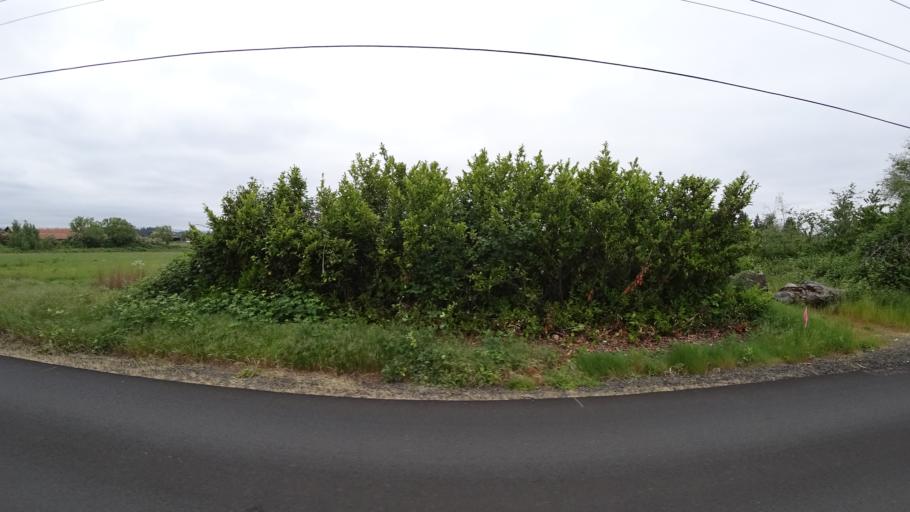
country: US
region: Oregon
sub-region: Washington County
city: Aloha
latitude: 45.4900
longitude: -122.9126
